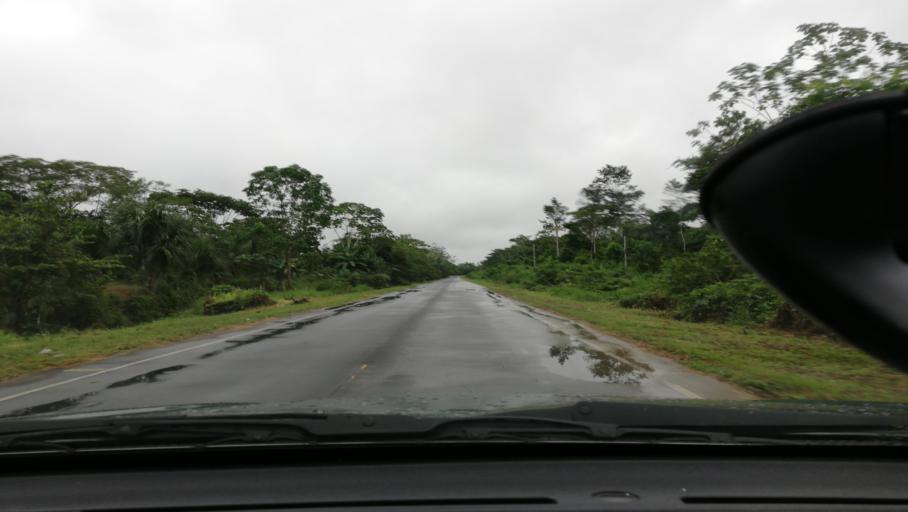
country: PE
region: Loreto
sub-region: Provincia de Maynas
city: San Juan
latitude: -4.0413
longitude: -73.4370
